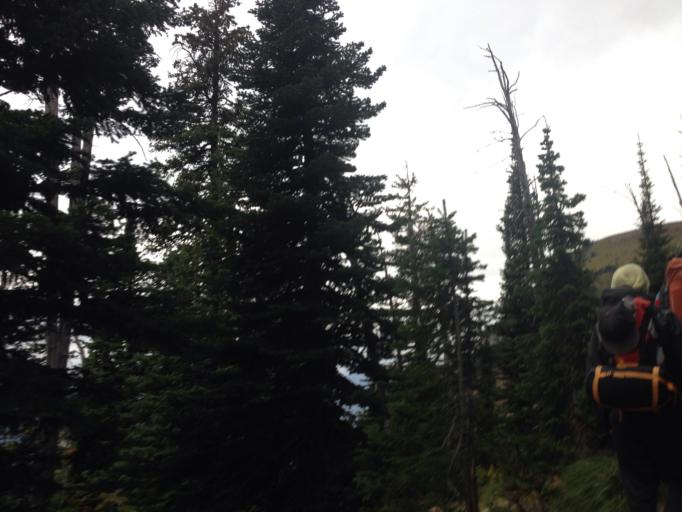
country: US
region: Montana
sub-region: Flathead County
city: Columbia Falls
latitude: 48.7221
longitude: -113.7216
